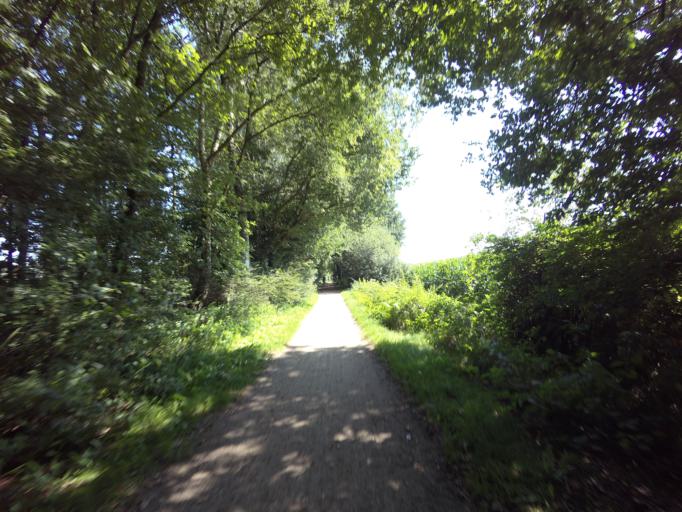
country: NL
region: Gelderland
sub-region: Berkelland
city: Neede
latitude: 52.1264
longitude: 6.6023
